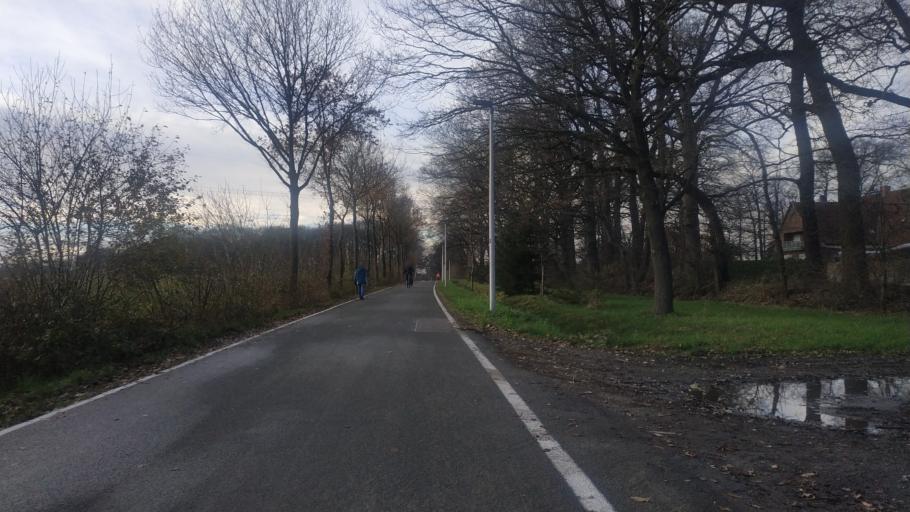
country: DE
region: North Rhine-Westphalia
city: Ibbenburen
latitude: 52.2689
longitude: 7.7524
